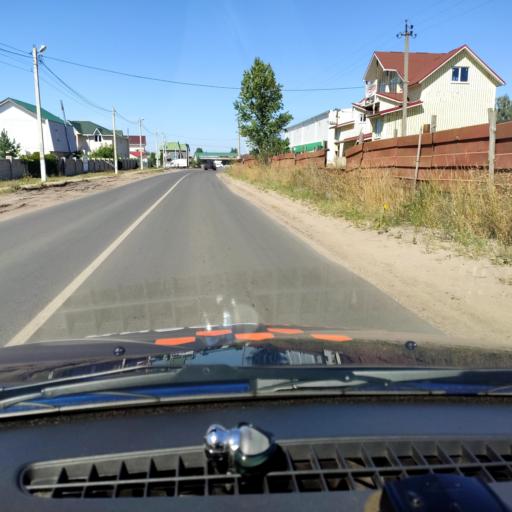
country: RU
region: Voronezj
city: Podgornoye
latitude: 51.7888
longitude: 39.1459
